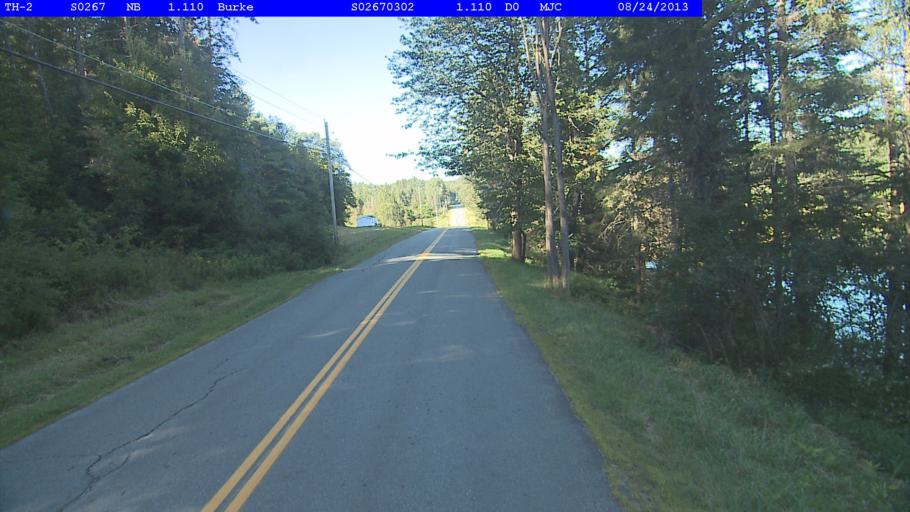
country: US
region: Vermont
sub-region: Caledonia County
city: Lyndonville
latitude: 44.6024
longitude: -71.9399
